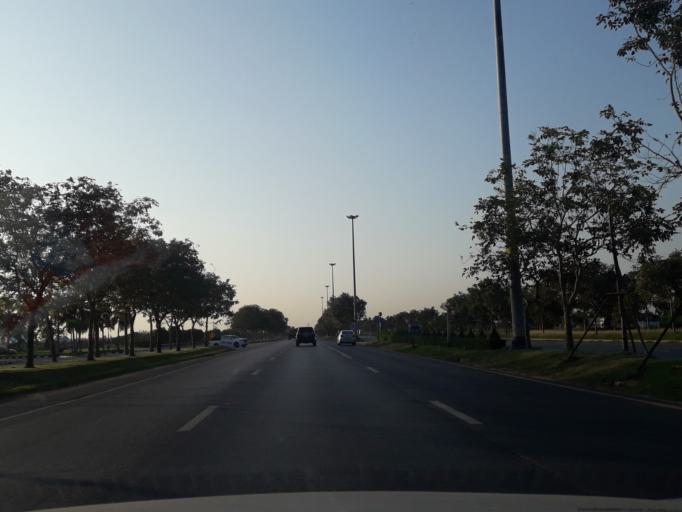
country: TH
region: Phra Nakhon Si Ayutthaya
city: Bang Pa-in
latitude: 14.2128
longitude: 100.5450
